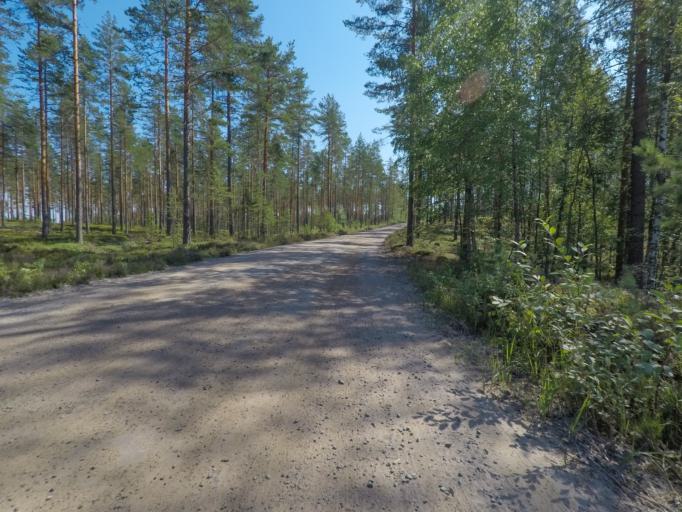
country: FI
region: Southern Savonia
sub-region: Mikkeli
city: Puumala
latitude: 61.4176
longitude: 28.0420
